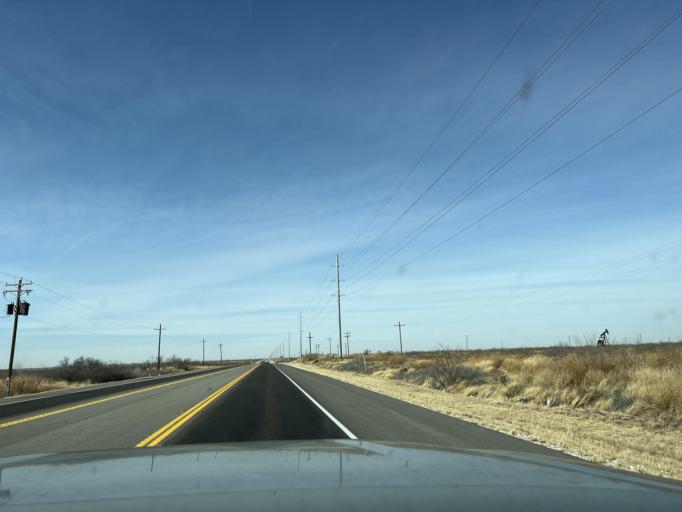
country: US
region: Texas
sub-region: Andrews County
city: Andrews
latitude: 32.3341
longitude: -102.6585
